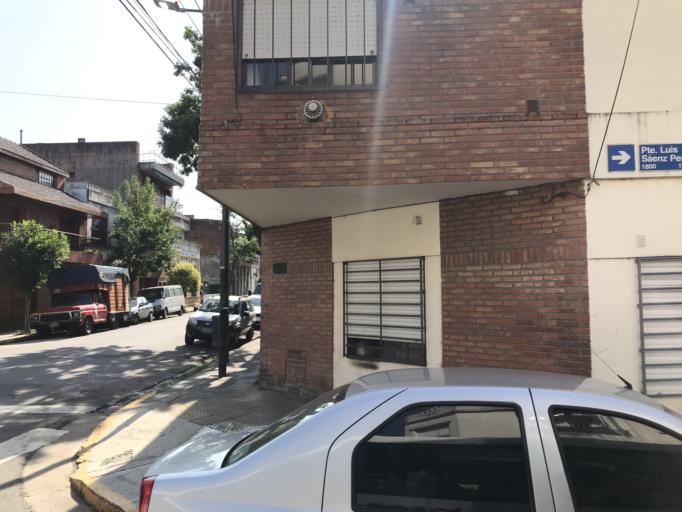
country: AR
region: Buenos Aires F.D.
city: Buenos Aires
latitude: -34.6300
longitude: -58.3869
